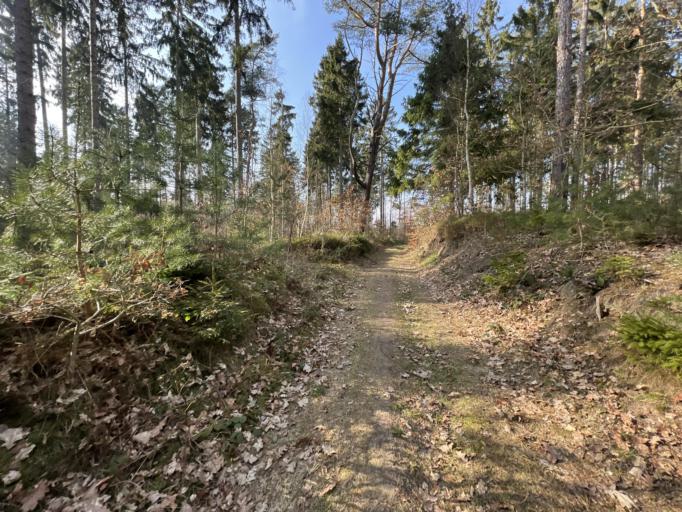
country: DE
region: Mecklenburg-Vorpommern
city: Sagard
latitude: 54.4791
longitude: 13.5578
